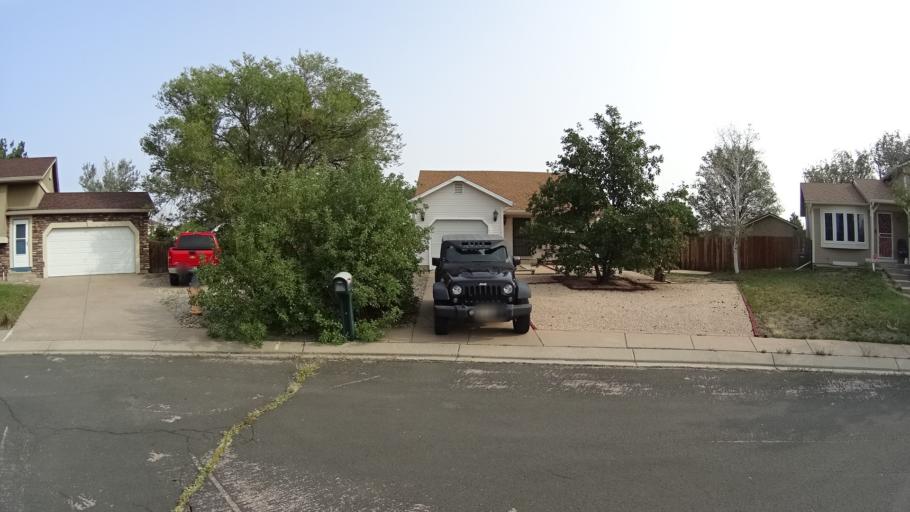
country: US
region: Colorado
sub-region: El Paso County
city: Stratmoor
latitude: 38.8082
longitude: -104.7452
